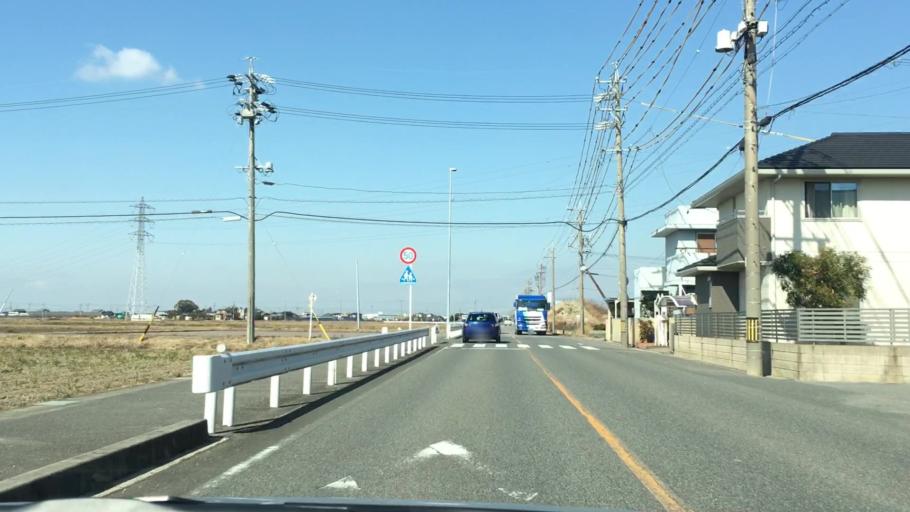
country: JP
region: Aichi
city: Anjo
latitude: 34.9808
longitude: 137.1186
